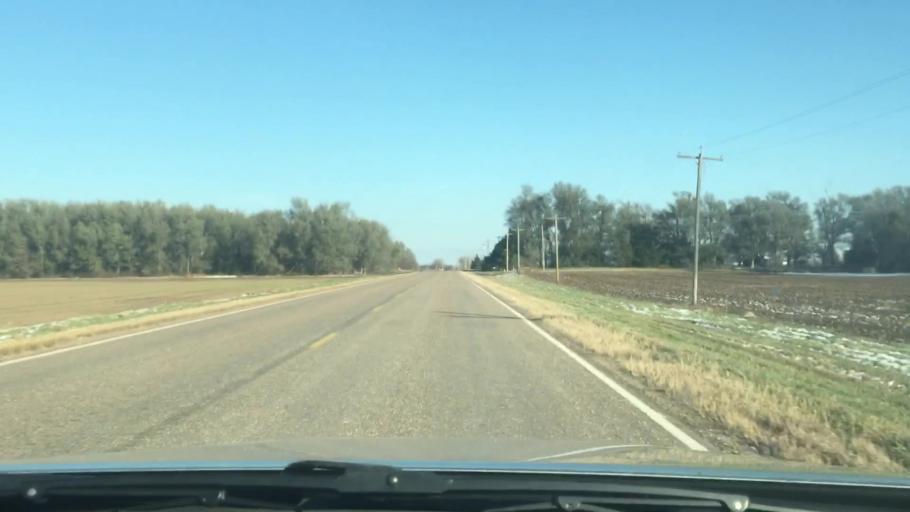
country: US
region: Kansas
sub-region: Rice County
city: Lyons
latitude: 38.2895
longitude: -98.1827
